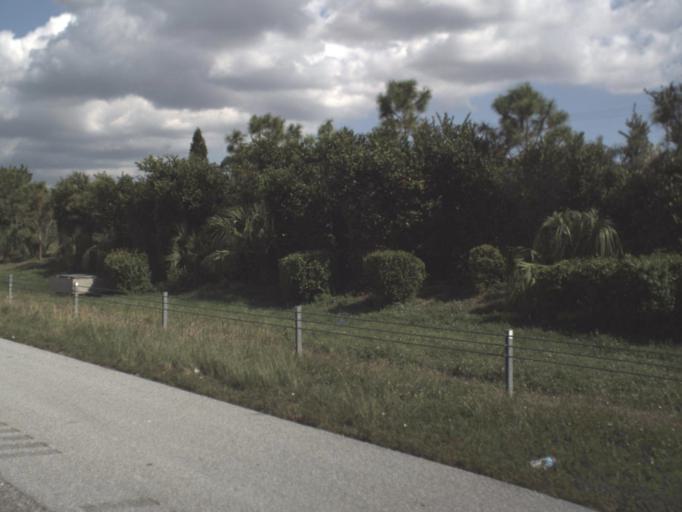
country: US
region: Florida
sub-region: Palm Beach County
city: Greenacres City
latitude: 26.5959
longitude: -80.1734
